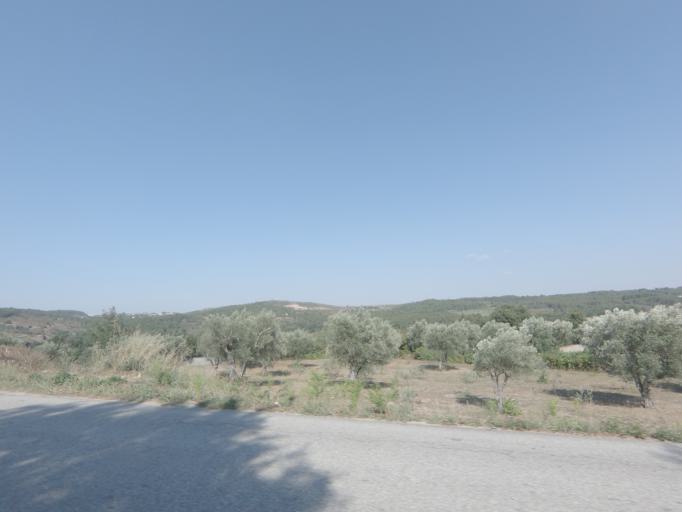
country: PT
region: Viseu
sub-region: Moimenta da Beira
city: Moimenta da Beira
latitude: 40.9746
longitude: -7.5912
